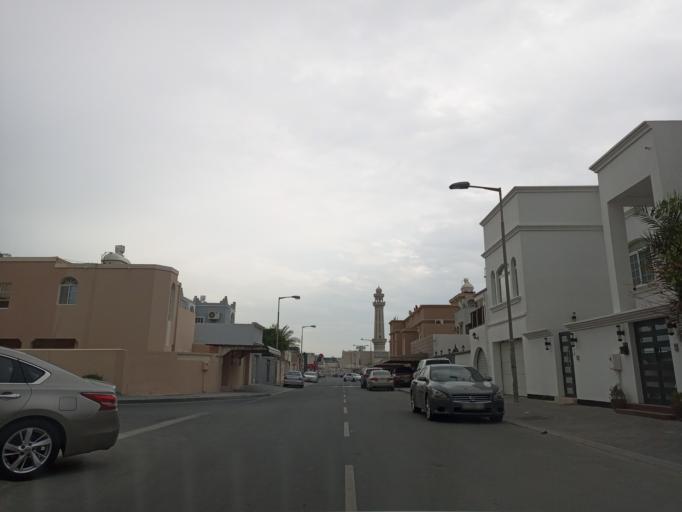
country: BH
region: Muharraq
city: Al Muharraq
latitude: 26.2596
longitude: 50.6317
